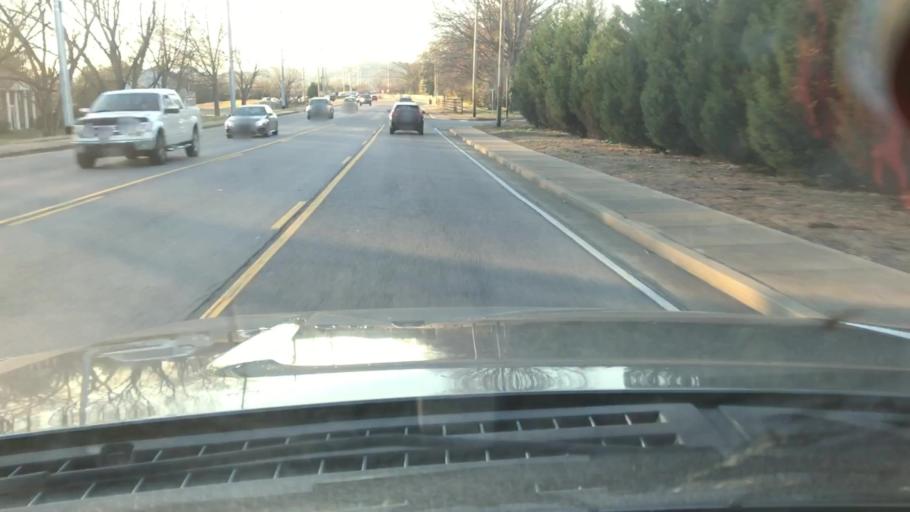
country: US
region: Tennessee
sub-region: Williamson County
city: Brentwood Estates
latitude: 35.9653
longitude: -86.7968
